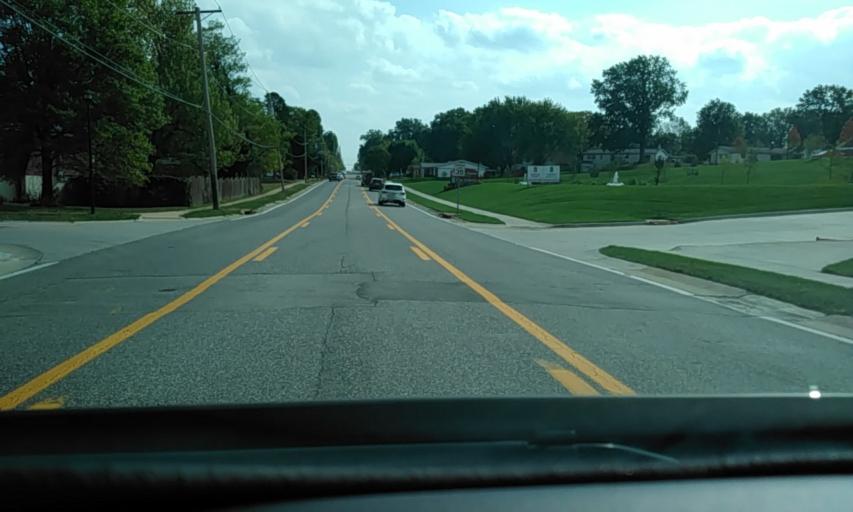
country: US
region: Missouri
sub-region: Saint Louis County
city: Concord
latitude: 38.5060
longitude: -90.3685
